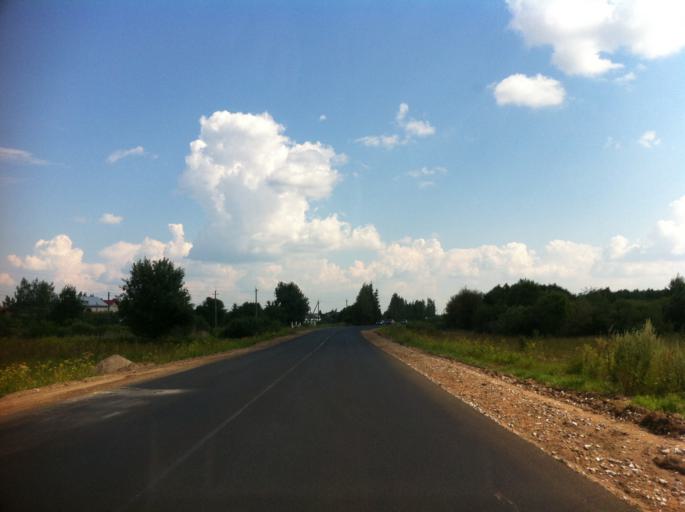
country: RU
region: Pskov
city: Pskov
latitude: 57.8223
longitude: 28.1431
